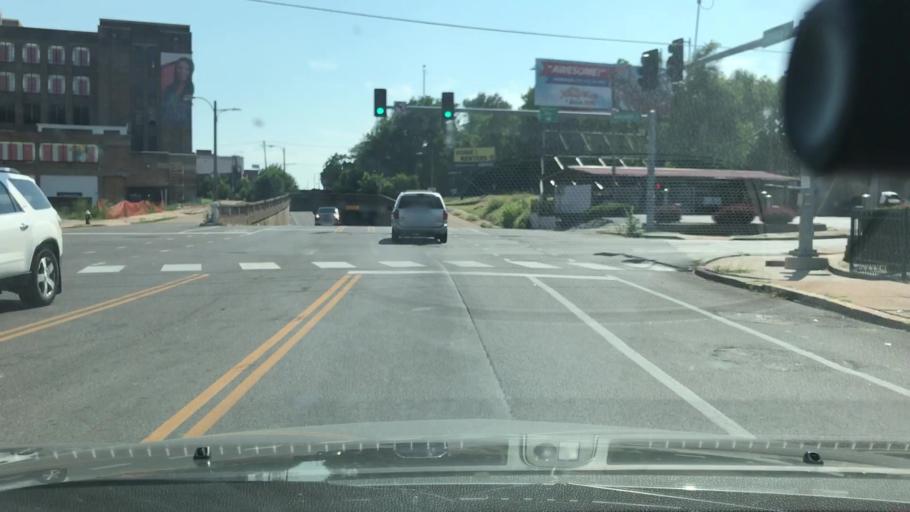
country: US
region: Missouri
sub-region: Saint Louis County
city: Lemay
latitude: 38.5884
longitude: -90.2582
